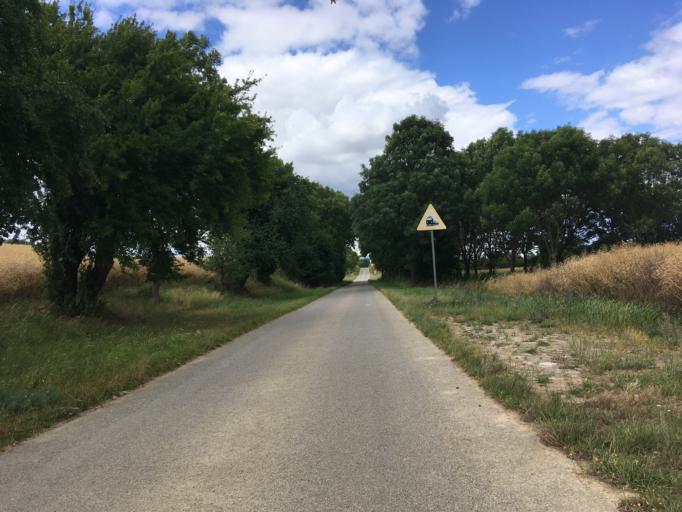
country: DE
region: Brandenburg
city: Gramzow
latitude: 53.2591
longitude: 14.0155
